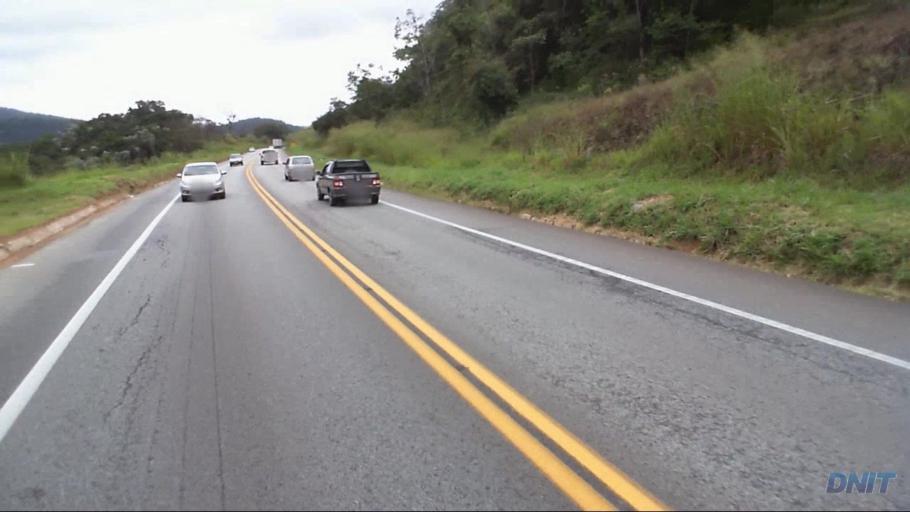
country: BR
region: Minas Gerais
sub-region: Joao Monlevade
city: Joao Monlevade
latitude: -19.8540
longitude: -43.1323
